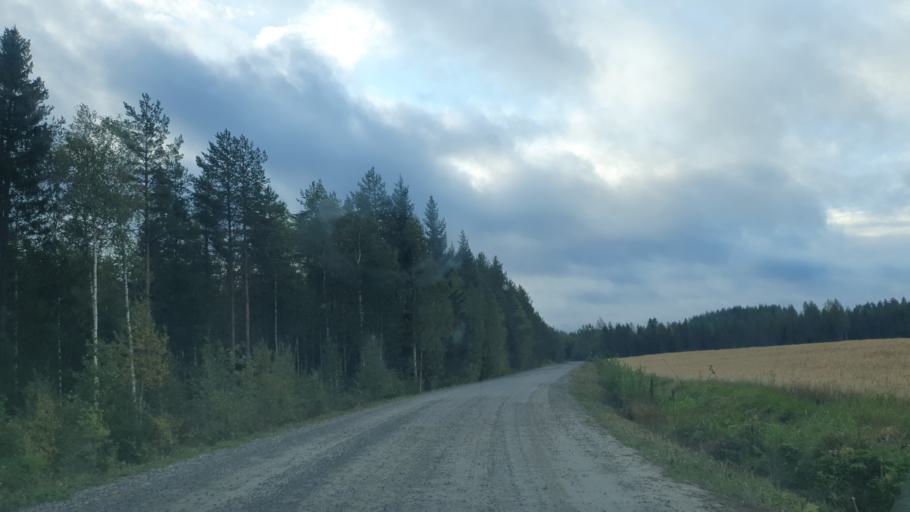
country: FI
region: Kainuu
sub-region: Kehys-Kainuu
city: Kuhmo
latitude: 64.1339
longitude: 29.5807
